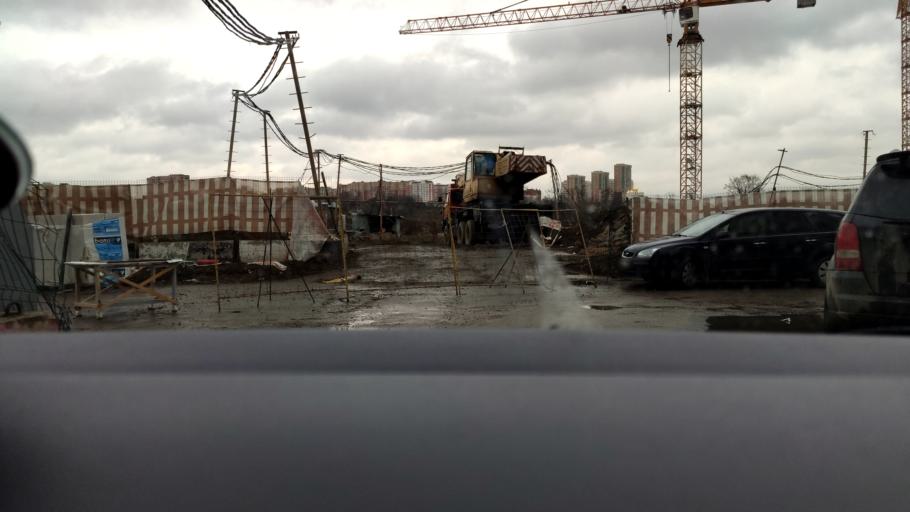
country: RU
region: Moskovskaya
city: Pavshino
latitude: 55.8601
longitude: 37.3736
